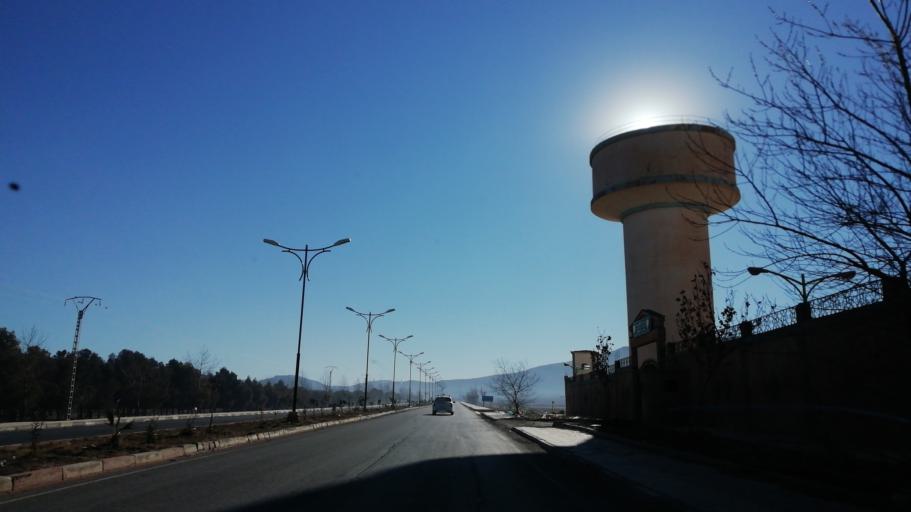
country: DZ
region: El Bayadh
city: El Bayadh
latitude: 33.6651
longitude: 1.0488
